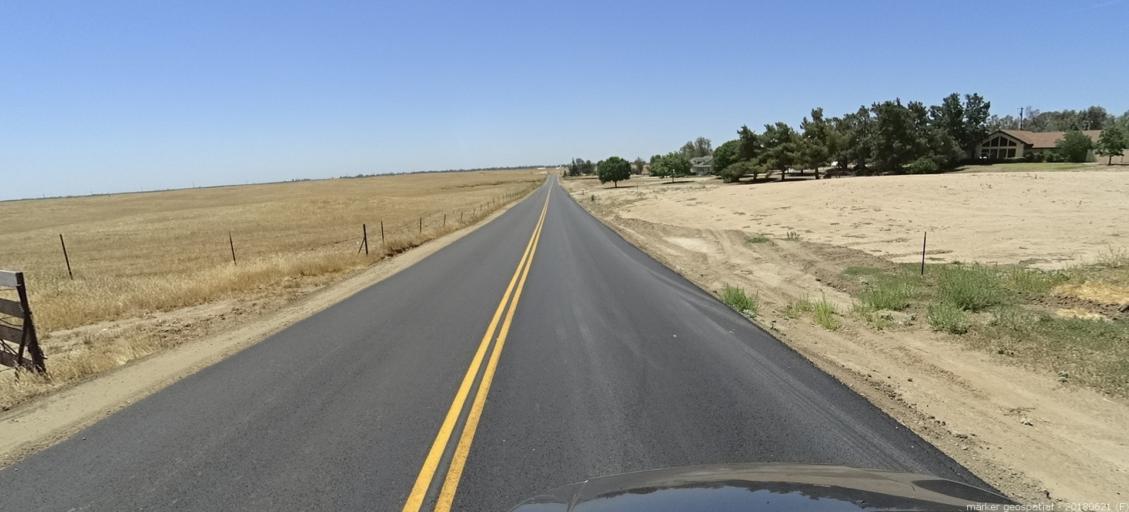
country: US
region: California
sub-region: Madera County
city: Bonadelle Ranchos-Madera Ranchos
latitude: 36.9716
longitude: -119.8759
